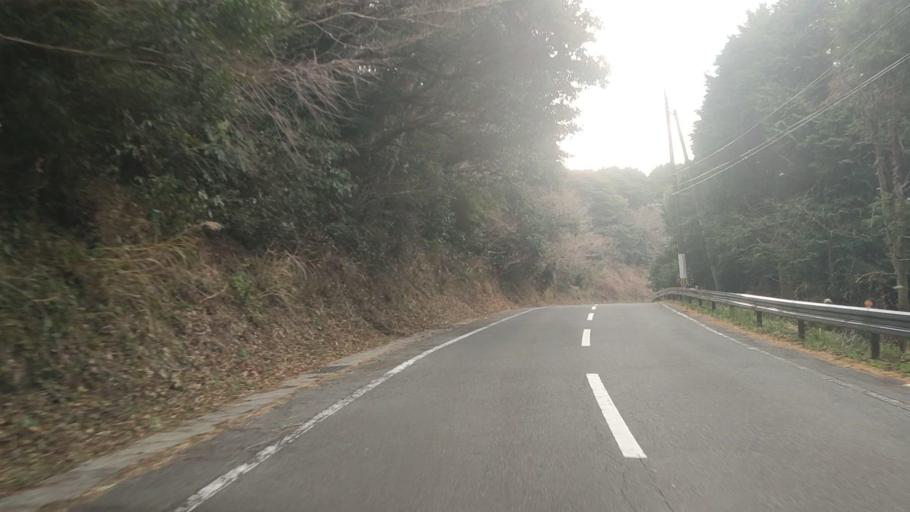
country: JP
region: Nagasaki
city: Shimabara
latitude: 32.7225
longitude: 130.2496
